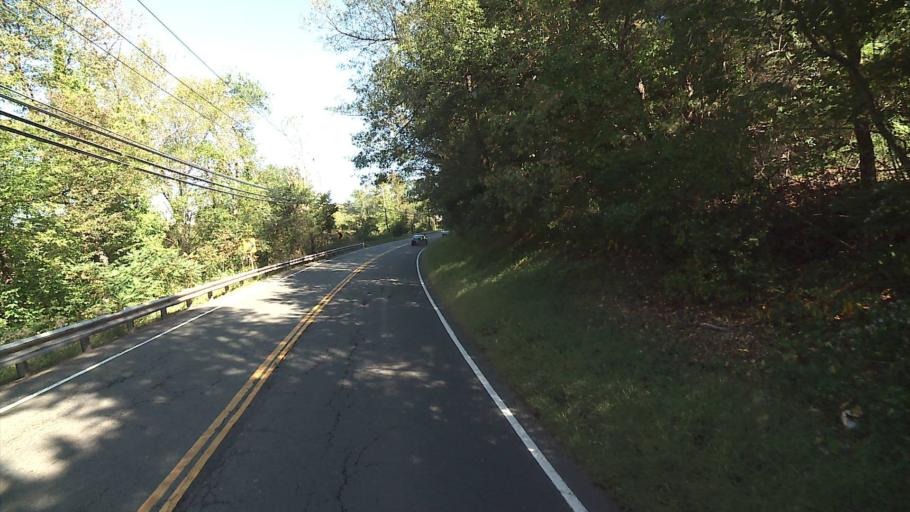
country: US
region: Connecticut
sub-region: Tolland County
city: Ellington
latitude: 41.9299
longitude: -72.4561
